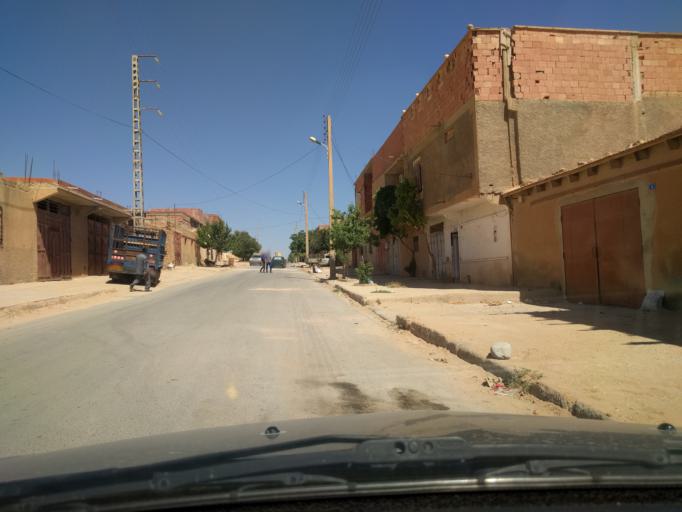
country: DZ
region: Tiaret
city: Frenda
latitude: 34.8907
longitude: 1.2444
